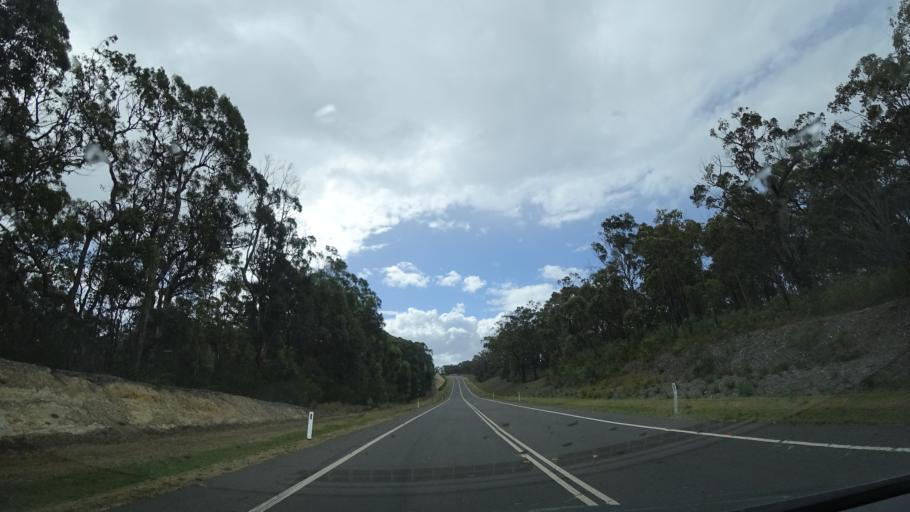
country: AU
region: New South Wales
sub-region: Wyong Shire
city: Kingfisher Shores
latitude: -33.1622
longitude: 151.6176
